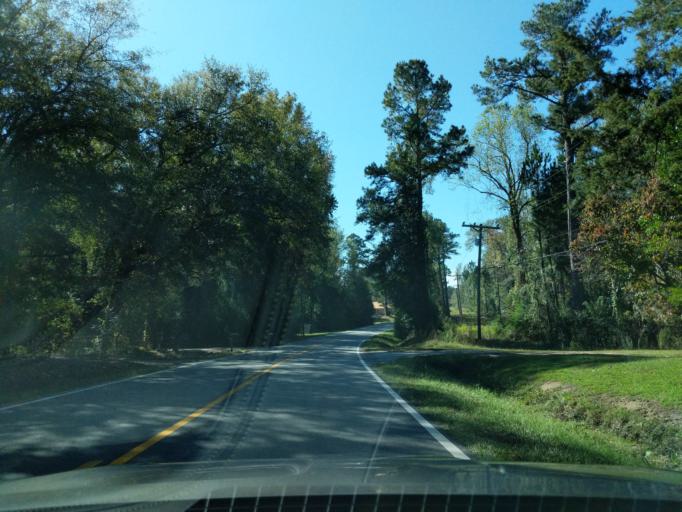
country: US
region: Georgia
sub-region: Richmond County
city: Hephzibah
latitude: 33.3020
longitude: -82.0193
